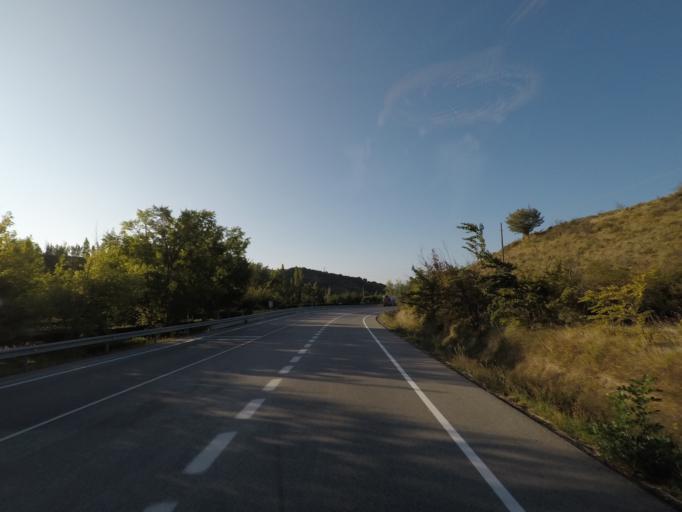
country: ES
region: Navarre
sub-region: Provincia de Navarra
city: Liedena
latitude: 42.6123
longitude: -1.2778
